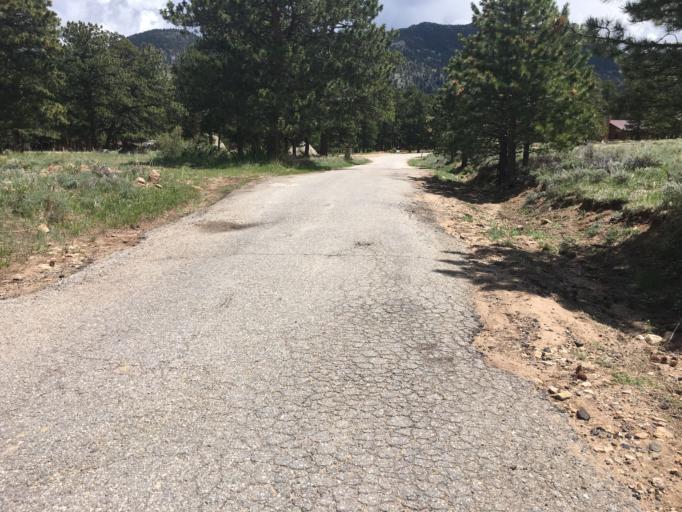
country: US
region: Colorado
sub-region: Larimer County
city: Estes Park
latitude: 40.3426
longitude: -105.5808
